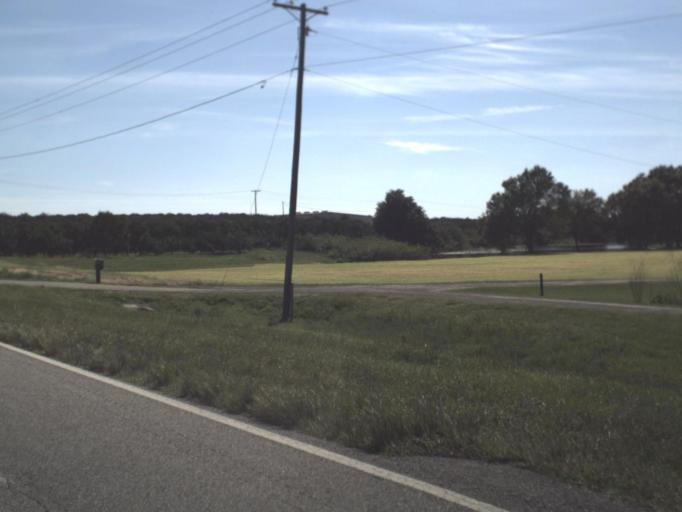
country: US
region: Florida
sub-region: Highlands County
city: Lake Placid
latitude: 27.3443
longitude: -81.3870
